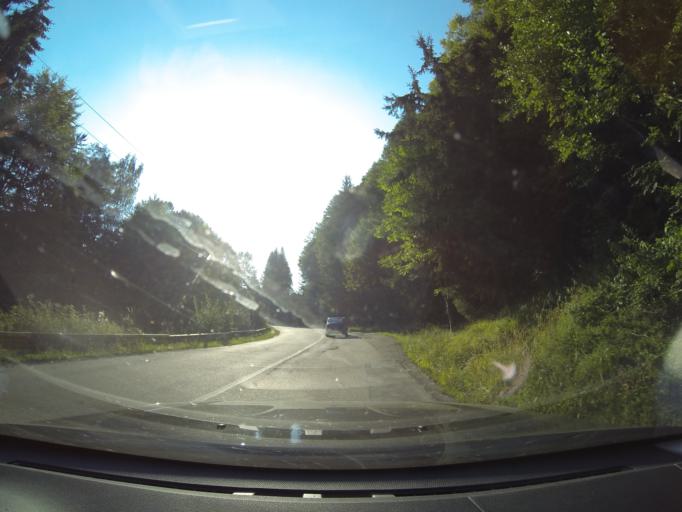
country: RO
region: Arges
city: Poenari
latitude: 45.3712
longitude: 24.6528
